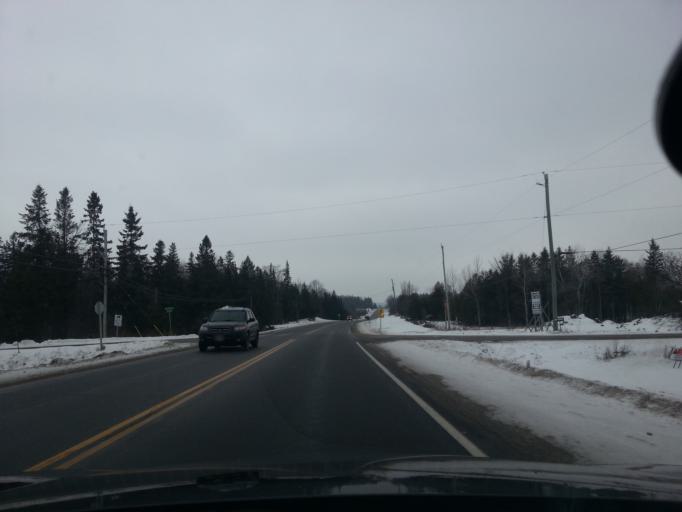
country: CA
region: Ontario
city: Carleton Place
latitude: 45.2458
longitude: -76.1651
